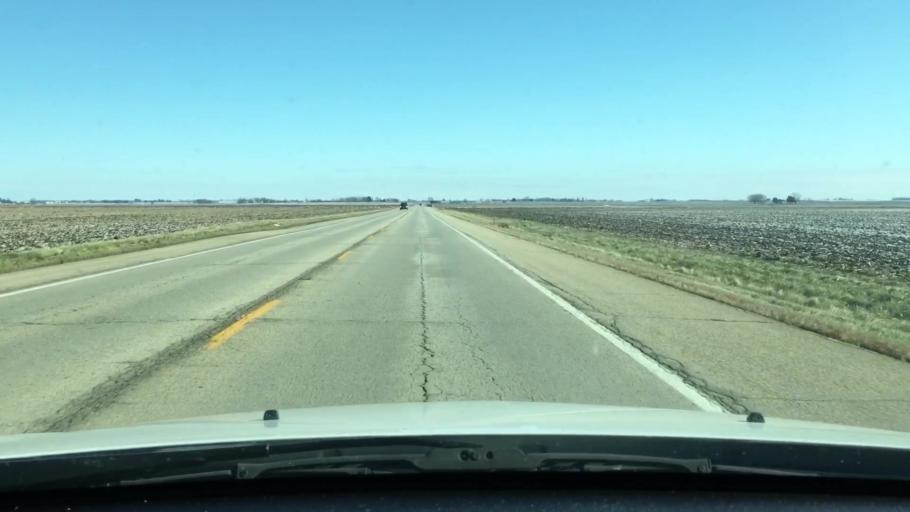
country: US
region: Illinois
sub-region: Ogle County
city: Hillcrest
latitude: 42.0076
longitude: -88.9767
